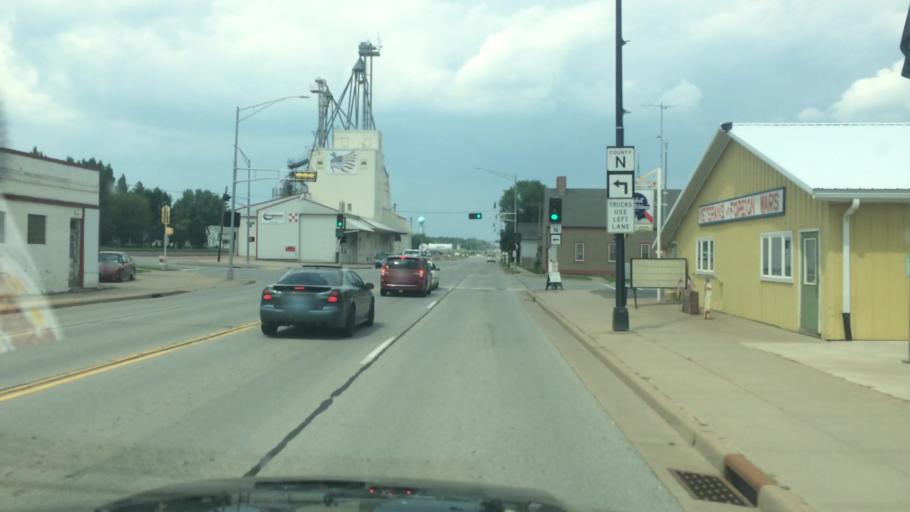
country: US
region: Wisconsin
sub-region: Clark County
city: Colby
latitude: 44.9090
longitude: -90.3153
